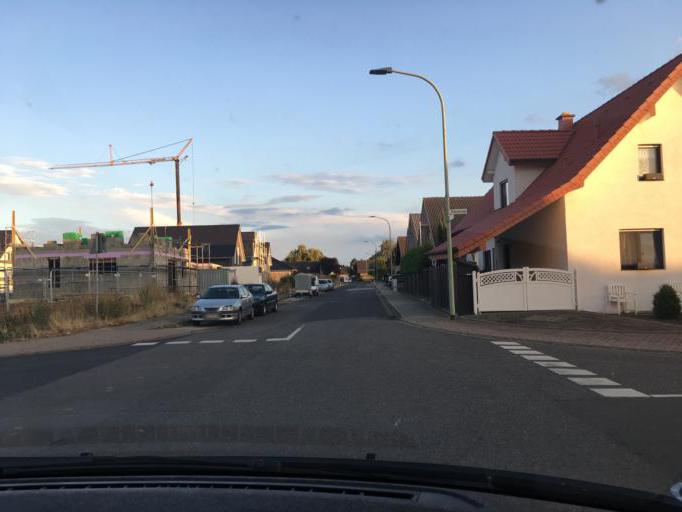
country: DE
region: North Rhine-Westphalia
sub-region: Regierungsbezirk Koln
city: Niederzier
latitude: 50.8717
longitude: 6.4709
